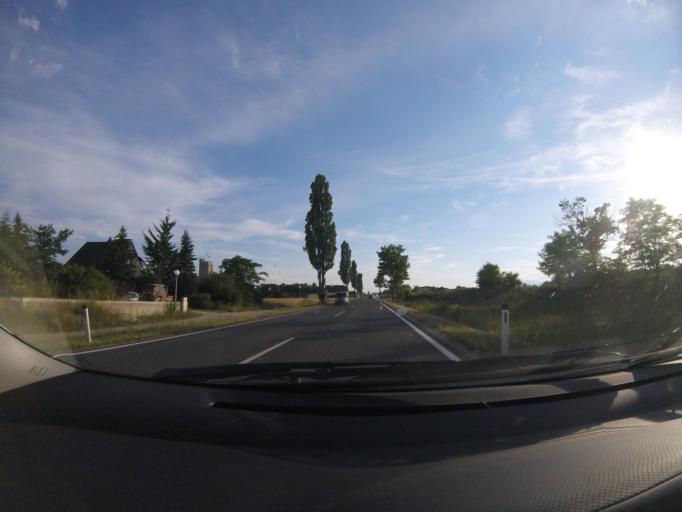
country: AT
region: Lower Austria
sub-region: Politischer Bezirk Wiener Neustadt
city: Lichtenworth
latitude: 47.8428
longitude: 16.2855
